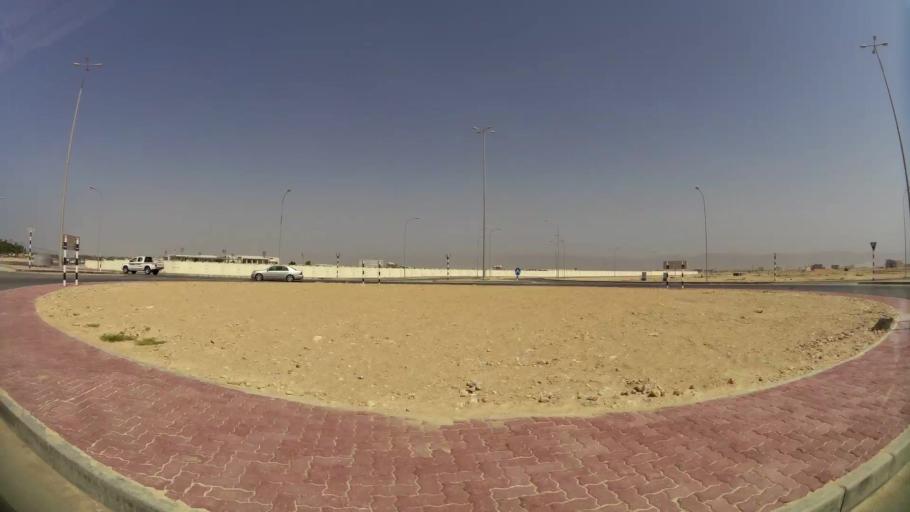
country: OM
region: Zufar
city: Salalah
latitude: 17.0310
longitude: 54.1361
